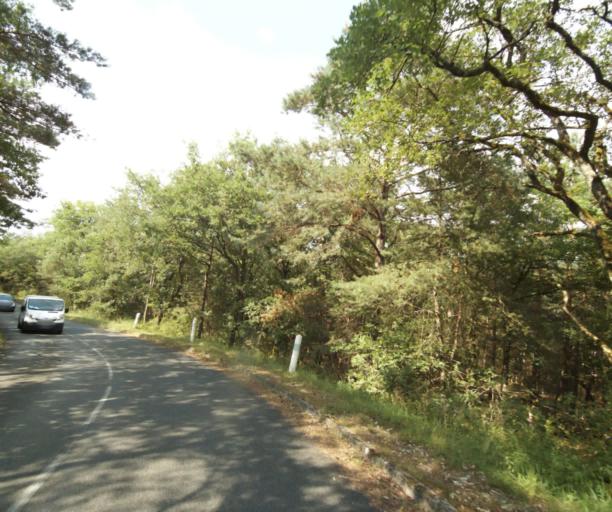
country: FR
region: Ile-de-France
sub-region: Departement de Seine-et-Marne
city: Arbonne-la-Foret
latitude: 48.3863
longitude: 2.5624
